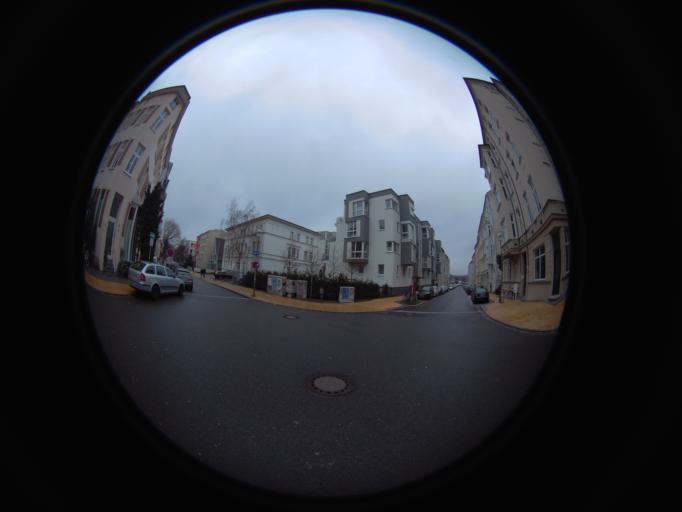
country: DE
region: Mecklenburg-Vorpommern
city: Rostock
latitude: 54.0904
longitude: 12.1248
